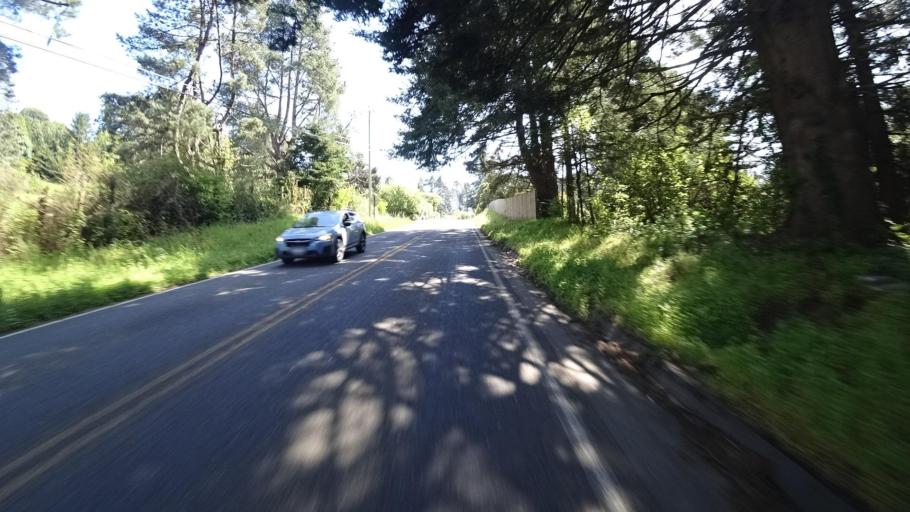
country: US
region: California
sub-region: Humboldt County
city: Hydesville
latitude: 40.5543
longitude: -124.1048
